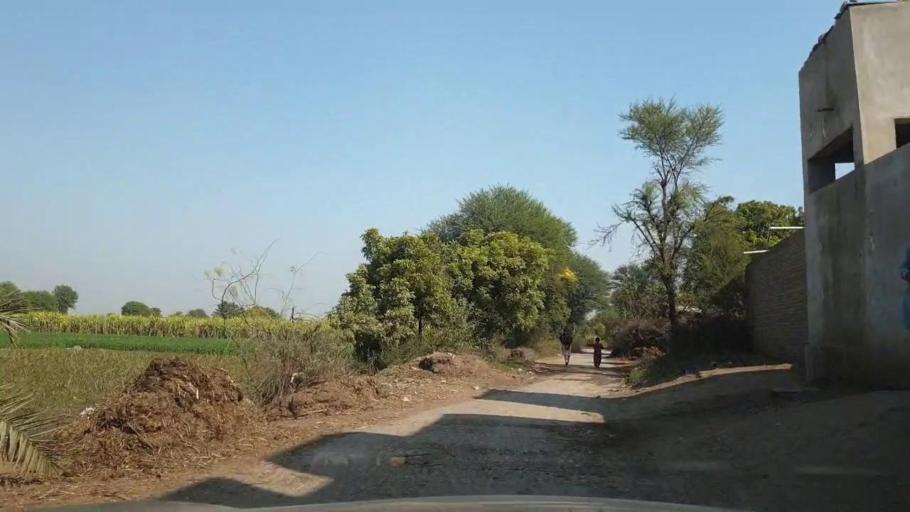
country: PK
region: Sindh
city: Tando Allahyar
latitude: 25.5732
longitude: 68.7317
